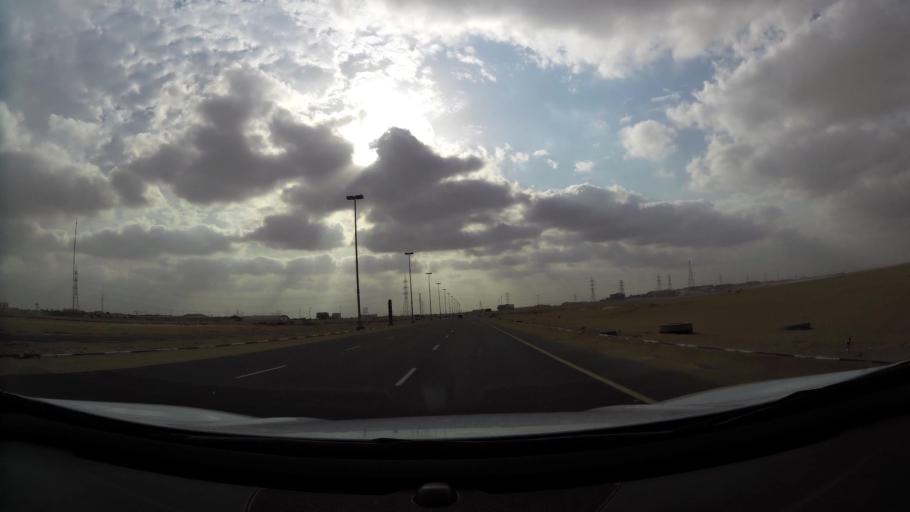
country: AE
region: Abu Dhabi
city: Abu Dhabi
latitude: 24.3460
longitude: 54.6015
